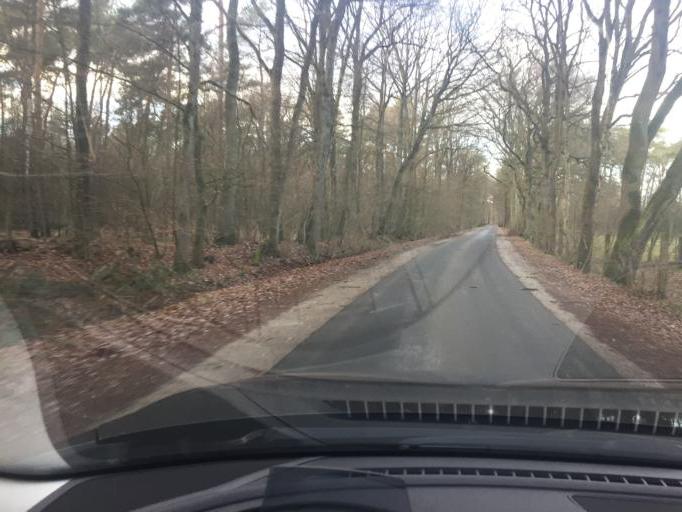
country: DE
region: North Rhine-Westphalia
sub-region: Regierungsbezirk Dusseldorf
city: Schermbeck
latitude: 51.6985
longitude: 6.8563
